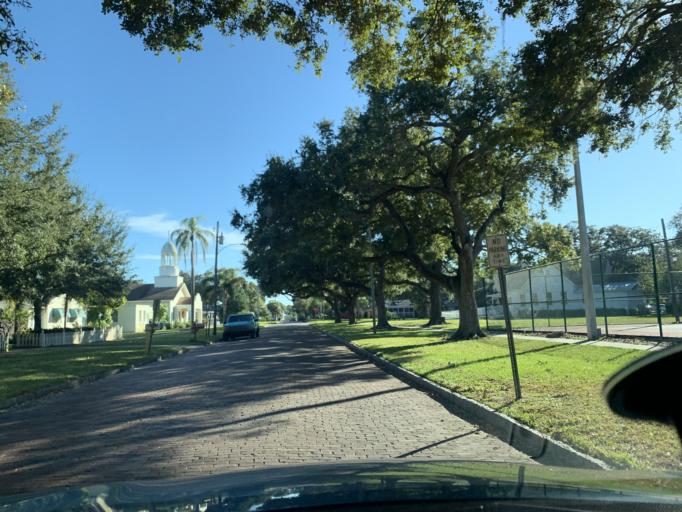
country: US
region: Florida
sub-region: Pinellas County
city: Gulfport
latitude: 27.7433
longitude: -82.7052
